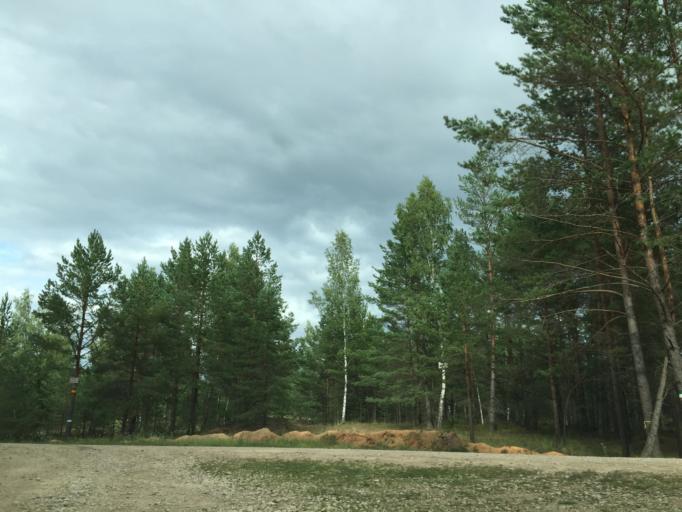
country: LV
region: Saulkrastu
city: Saulkrasti
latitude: 57.1801
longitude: 24.3784
